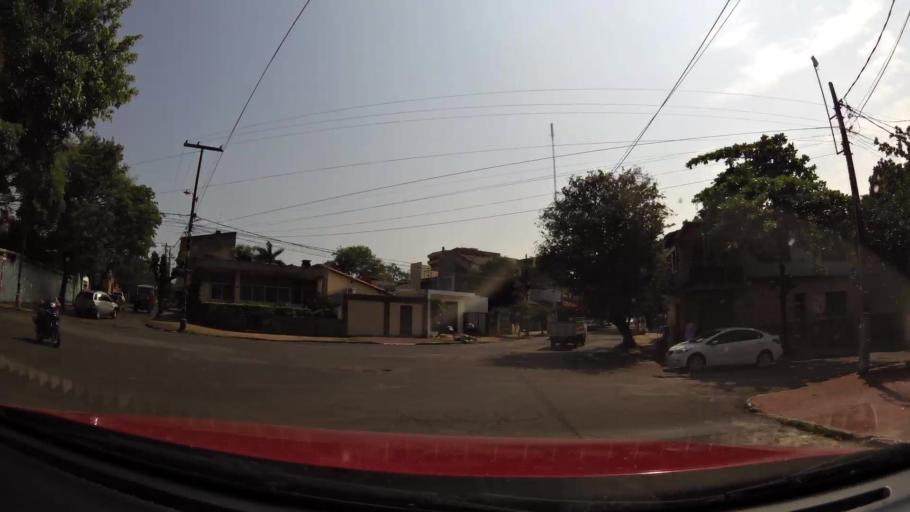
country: PY
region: Asuncion
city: Asuncion
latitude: -25.2906
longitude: -57.6526
